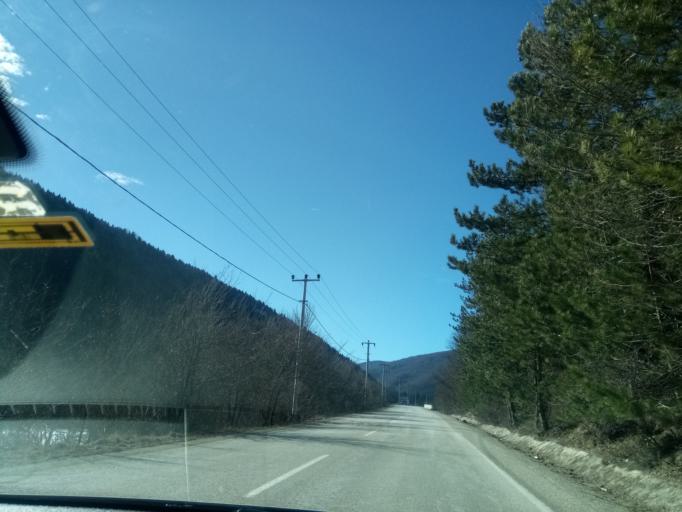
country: TR
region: Duzce
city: Kaynasli
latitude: 40.6627
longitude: 31.4125
